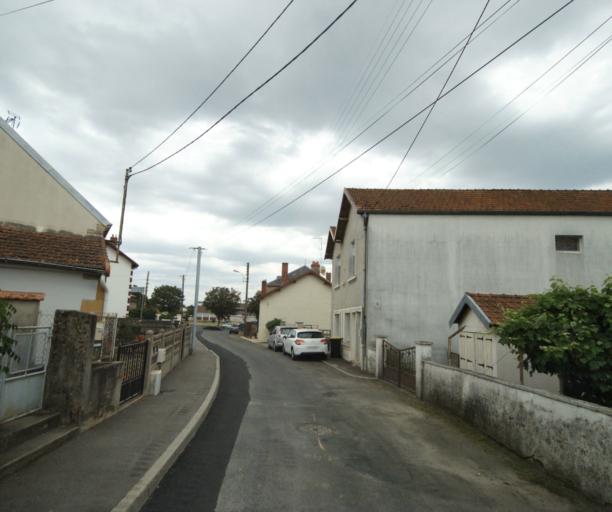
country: FR
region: Bourgogne
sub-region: Departement de Saone-et-Loire
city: Gueugnon
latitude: 46.6010
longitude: 4.0538
